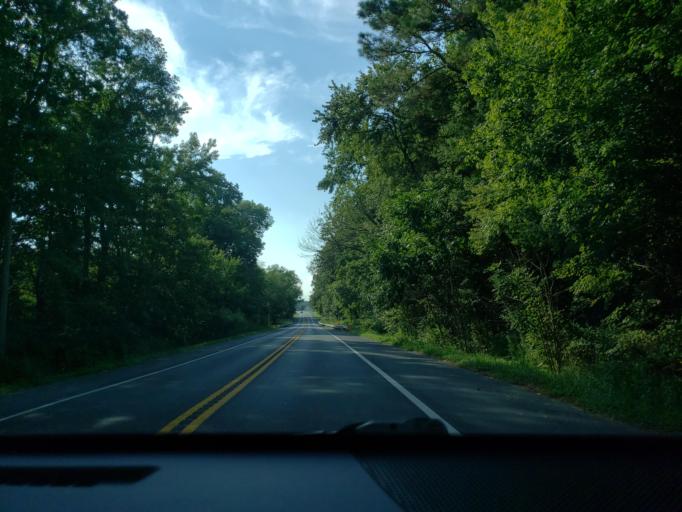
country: US
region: Delaware
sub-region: Sussex County
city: Milton
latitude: 38.7606
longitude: -75.2650
